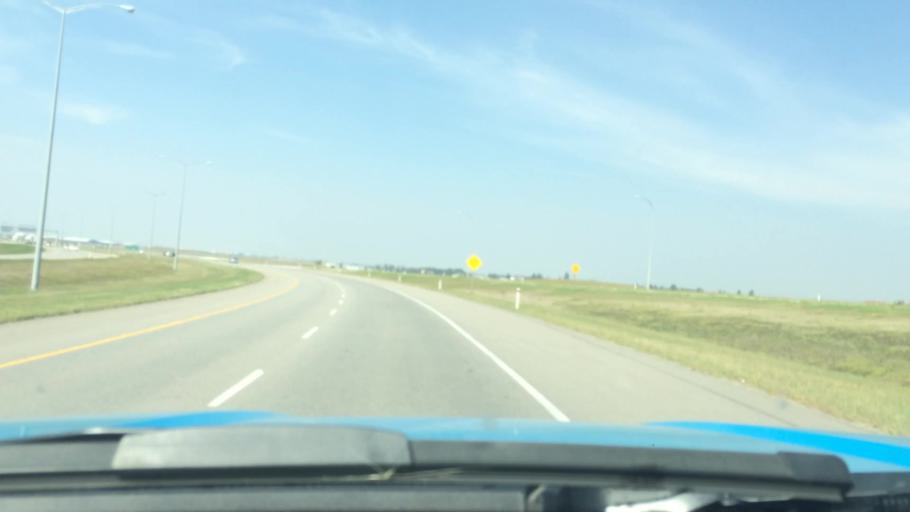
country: CA
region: Alberta
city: Chestermere
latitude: 50.9123
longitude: -113.9085
